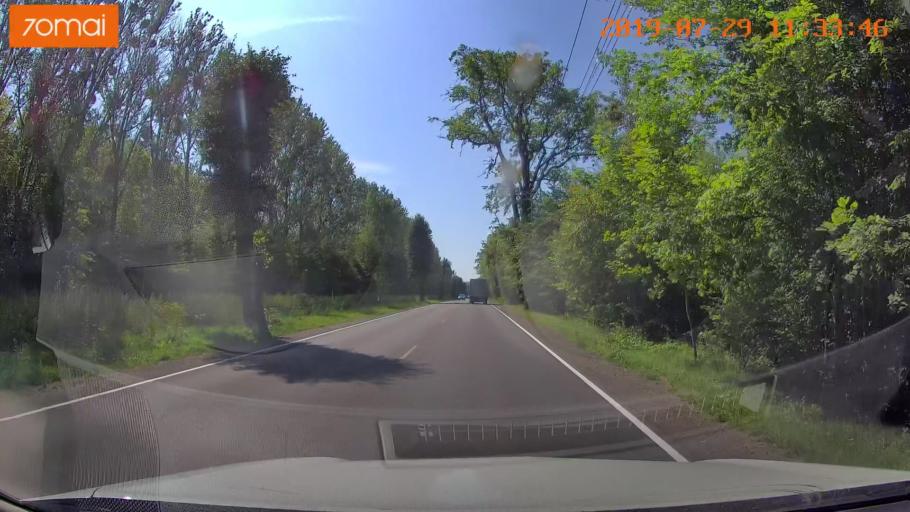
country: RU
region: Kaliningrad
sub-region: Gorod Kaliningrad
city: Kaliningrad
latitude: 54.6617
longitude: 20.5408
